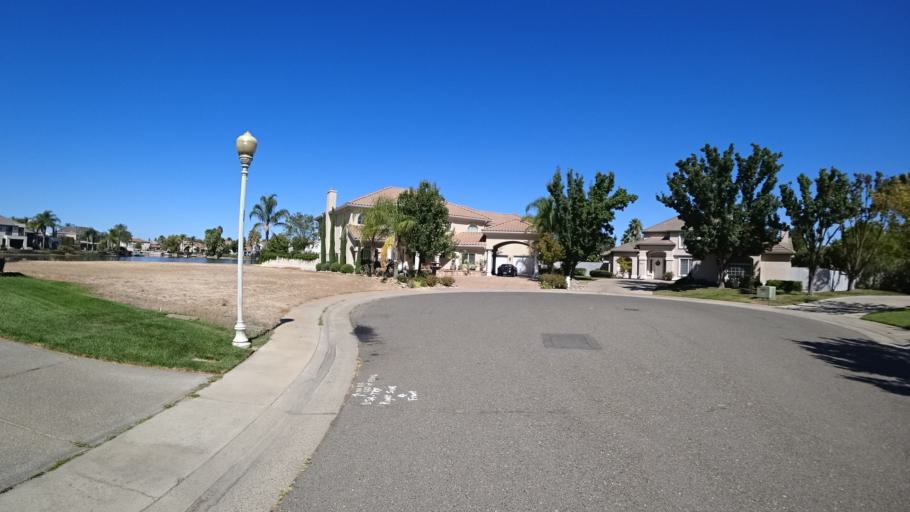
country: US
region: California
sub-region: Sacramento County
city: Laguna
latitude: 38.4193
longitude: -121.4655
